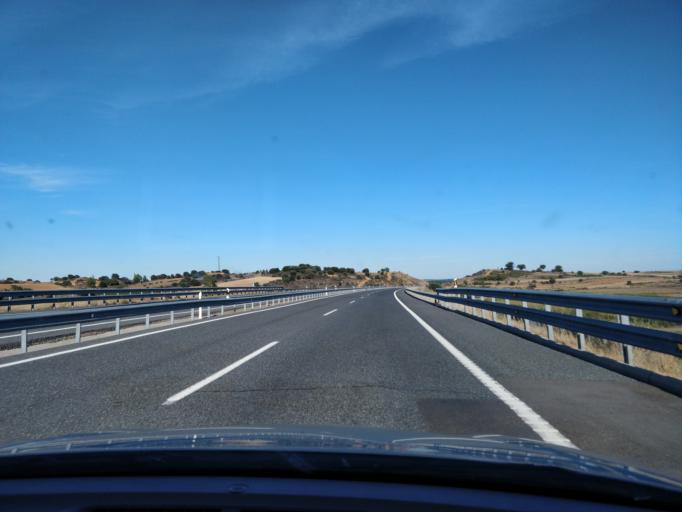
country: ES
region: Castille and Leon
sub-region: Provincia de Leon
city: Villarejo de Orbigo
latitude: 42.4451
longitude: -5.9432
